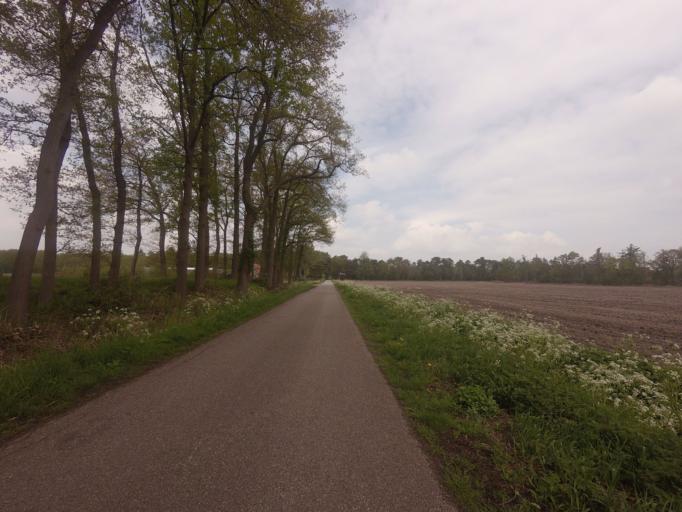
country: NL
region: Overijssel
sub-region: Gemeente Hof van Twente
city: Delden
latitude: 52.2352
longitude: 6.7251
